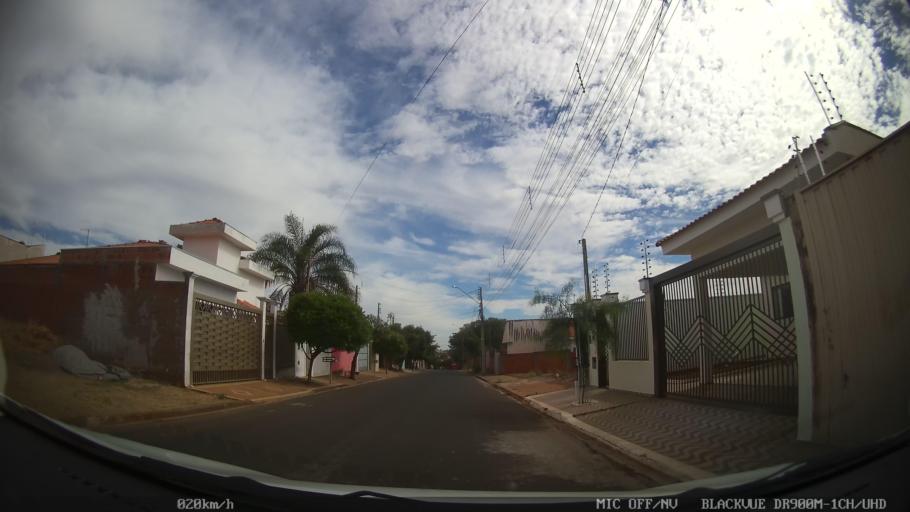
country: BR
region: Sao Paulo
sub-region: Catanduva
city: Catanduva
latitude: -21.1588
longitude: -48.9707
